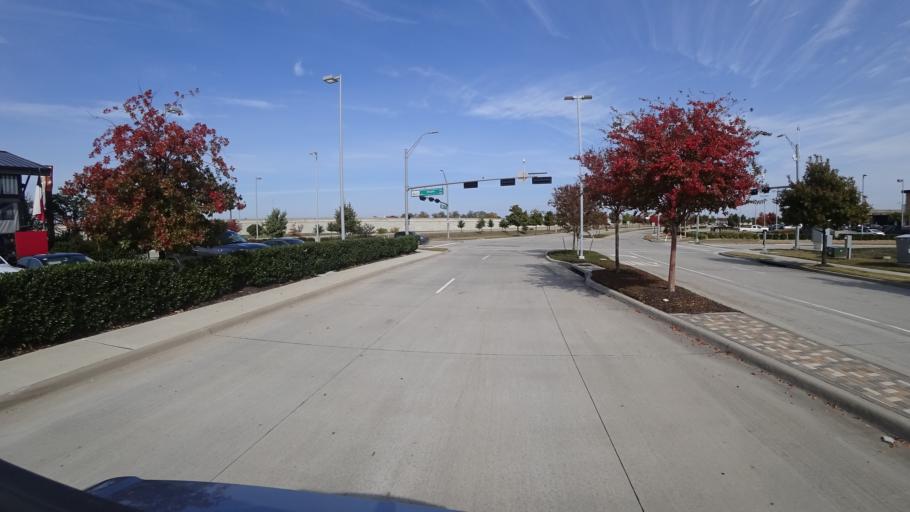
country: US
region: Texas
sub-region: Denton County
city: The Colony
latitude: 33.0713
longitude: -96.8730
